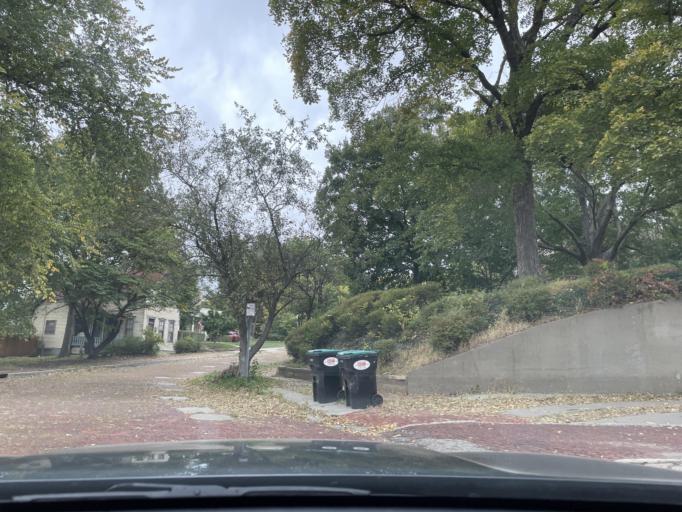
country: US
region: Missouri
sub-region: Buchanan County
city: Saint Joseph
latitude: 39.7710
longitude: -94.8506
